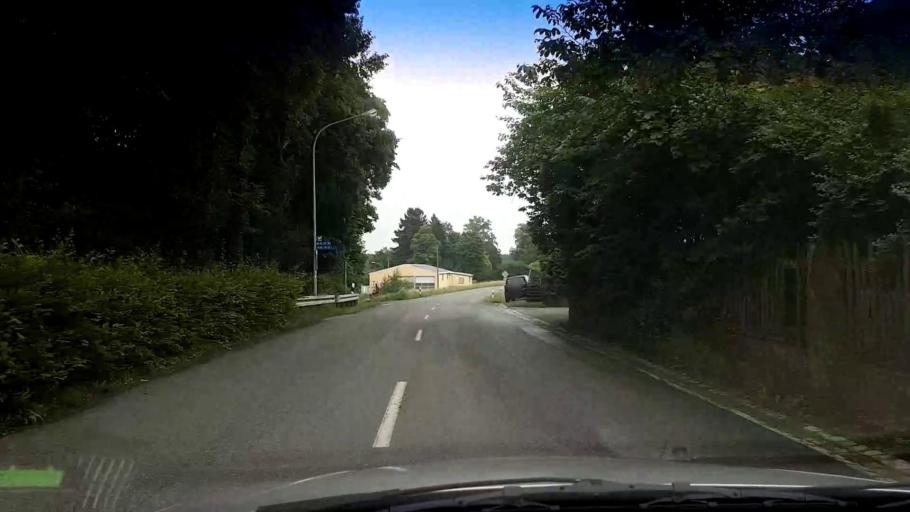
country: DE
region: Bavaria
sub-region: Upper Franconia
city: Kasendorf
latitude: 50.0772
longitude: 11.3210
